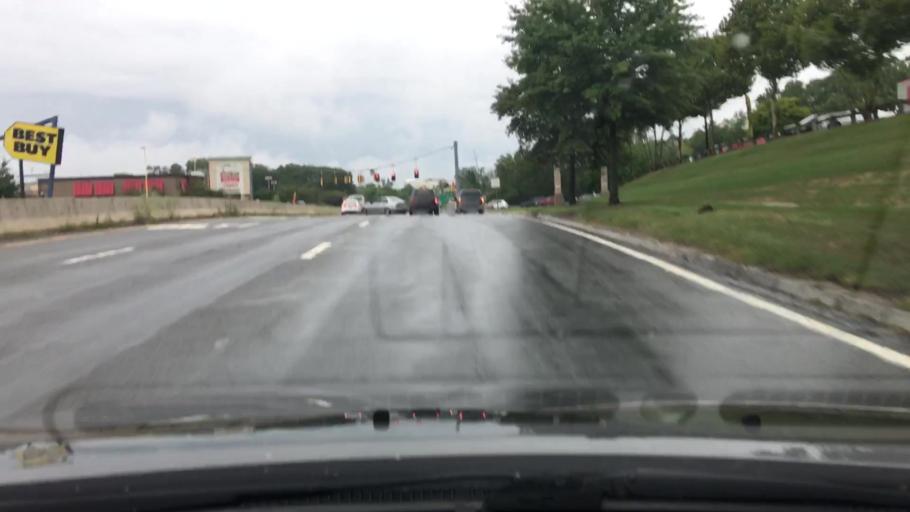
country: US
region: Rhode Island
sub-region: Providence County
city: Valley Falls
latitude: 41.9345
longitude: -71.3512
